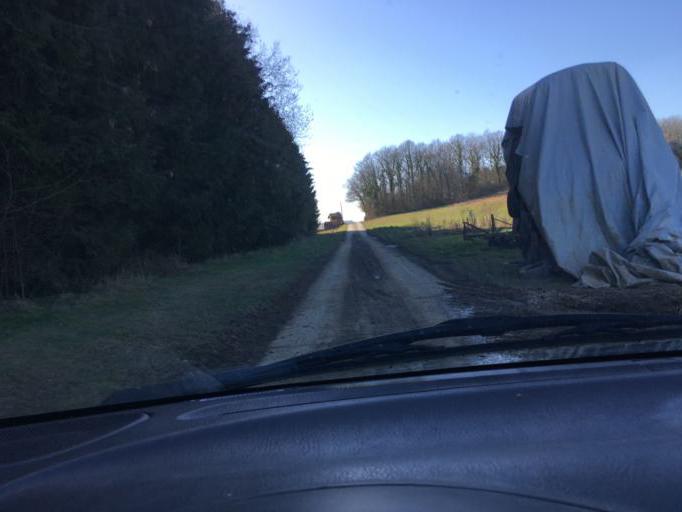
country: BE
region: Wallonia
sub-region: Province de Namur
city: Doische
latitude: 50.1207
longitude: 4.6735
